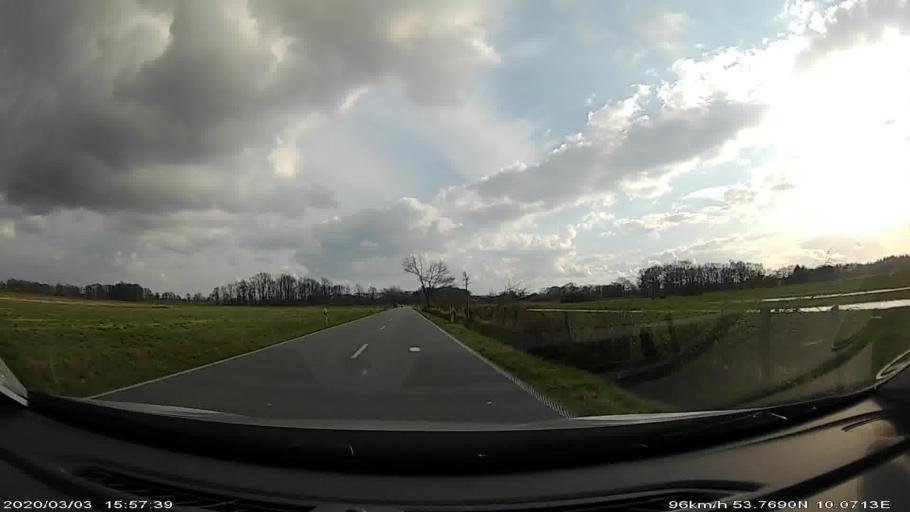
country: DE
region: Schleswig-Holstein
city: Tangstedt
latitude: 53.7708
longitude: 10.0713
